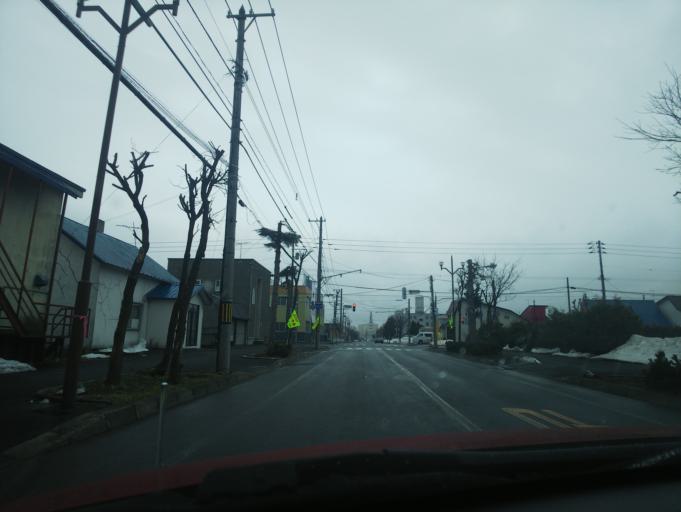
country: JP
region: Hokkaido
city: Nayoro
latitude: 44.3469
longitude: 142.4605
